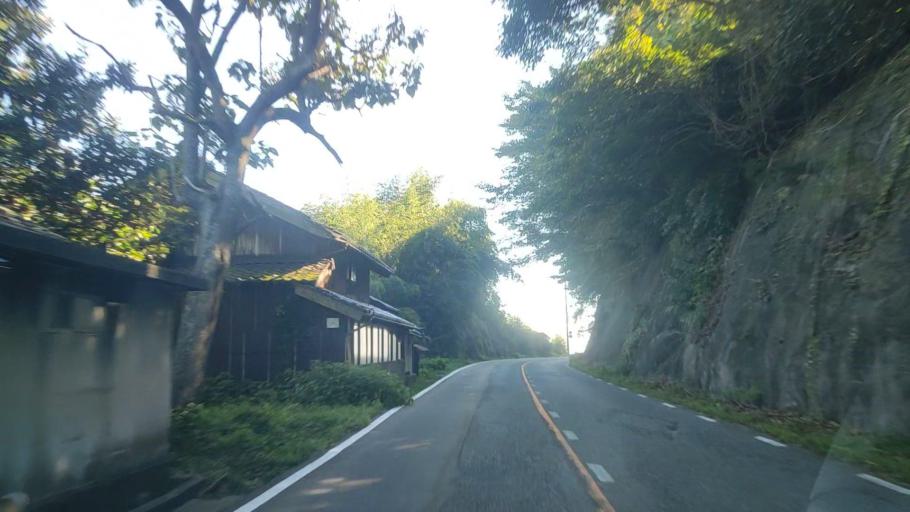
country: JP
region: Ishikawa
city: Nanao
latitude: 37.2739
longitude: 137.0969
